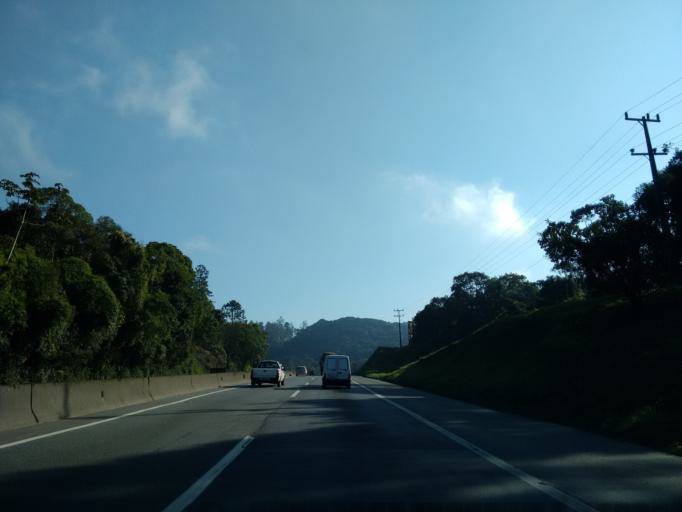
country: BR
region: Santa Catarina
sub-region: Joinville
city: Joinville
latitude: -26.2706
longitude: -48.8948
